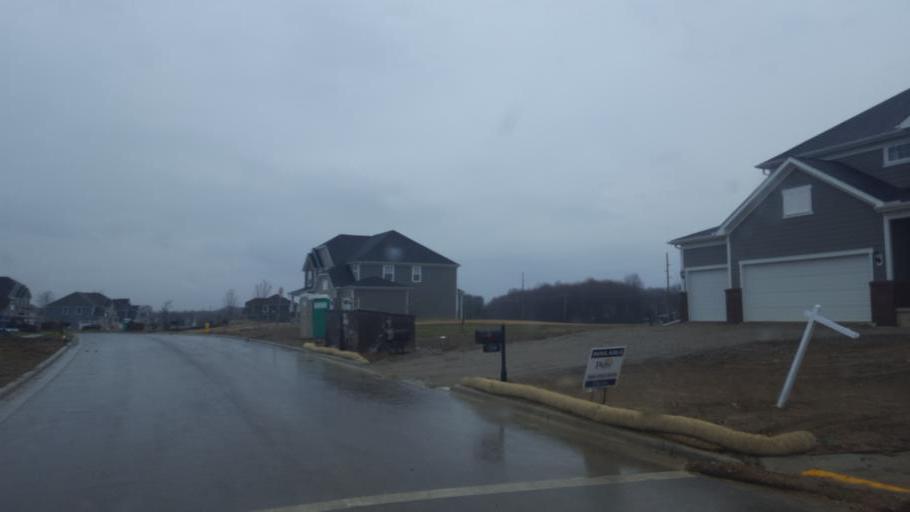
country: US
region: Ohio
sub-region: Delaware County
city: Lewis Center
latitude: 40.2572
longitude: -82.9475
